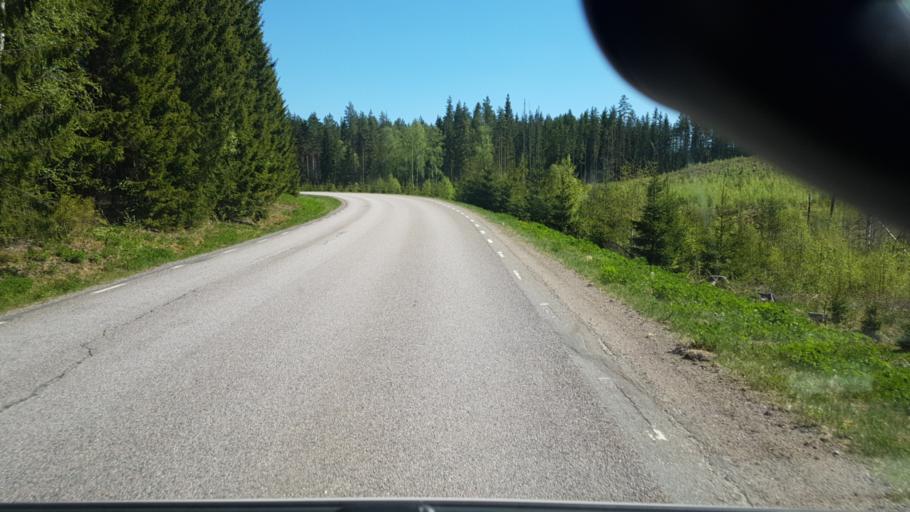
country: SE
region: Vaermland
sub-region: Eda Kommun
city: Charlottenberg
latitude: 59.8803
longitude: 12.3719
